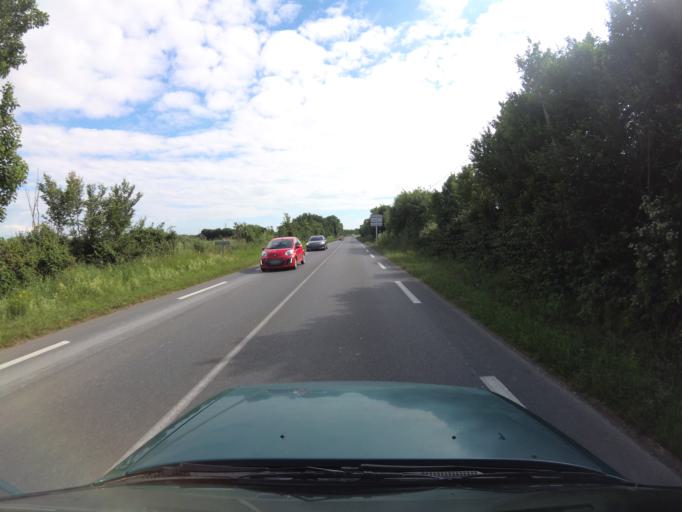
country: FR
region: Poitou-Charentes
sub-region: Departement de la Charente-Maritime
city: Saint-Xandre
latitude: 46.2221
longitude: -1.0855
